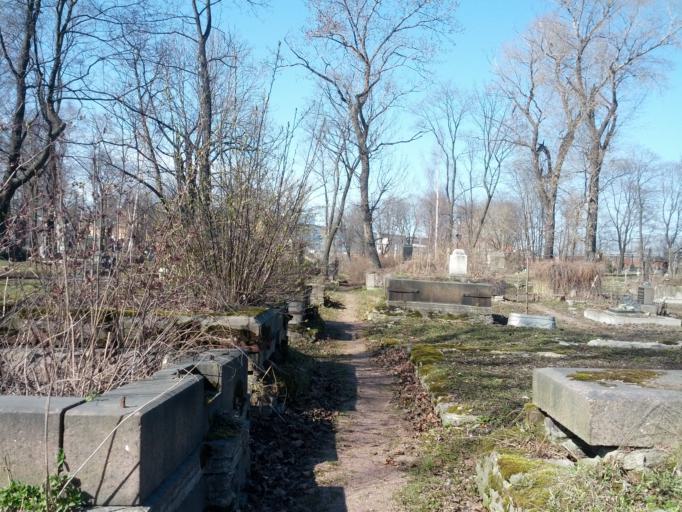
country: RU
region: St.-Petersburg
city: Centralniy
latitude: 59.9198
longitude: 30.3929
